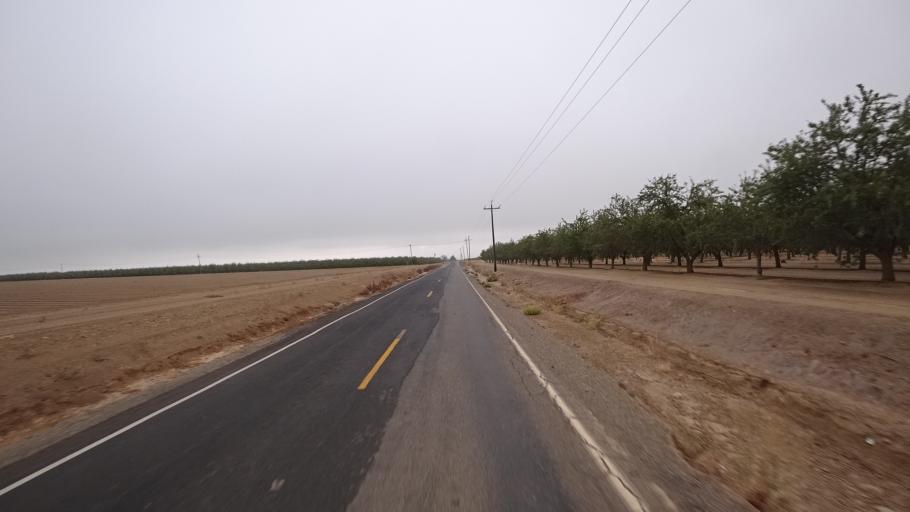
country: US
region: California
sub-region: Yolo County
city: Dunnigan
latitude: 38.9259
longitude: -122.0262
